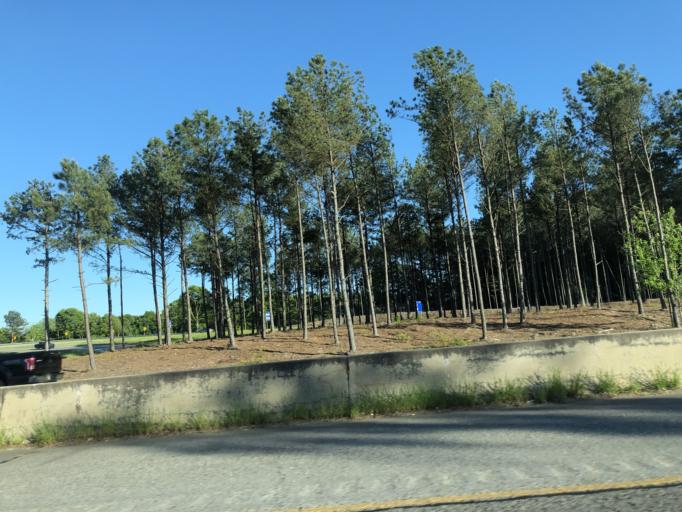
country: US
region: Georgia
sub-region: Oconee County
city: Bogart
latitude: 33.9390
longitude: -83.4631
